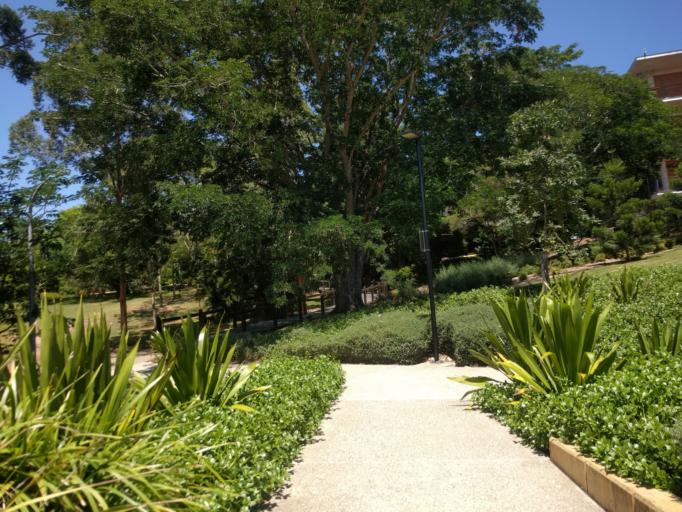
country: AU
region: Queensland
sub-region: Brisbane
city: South Brisbane
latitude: -27.4977
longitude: 153.0166
